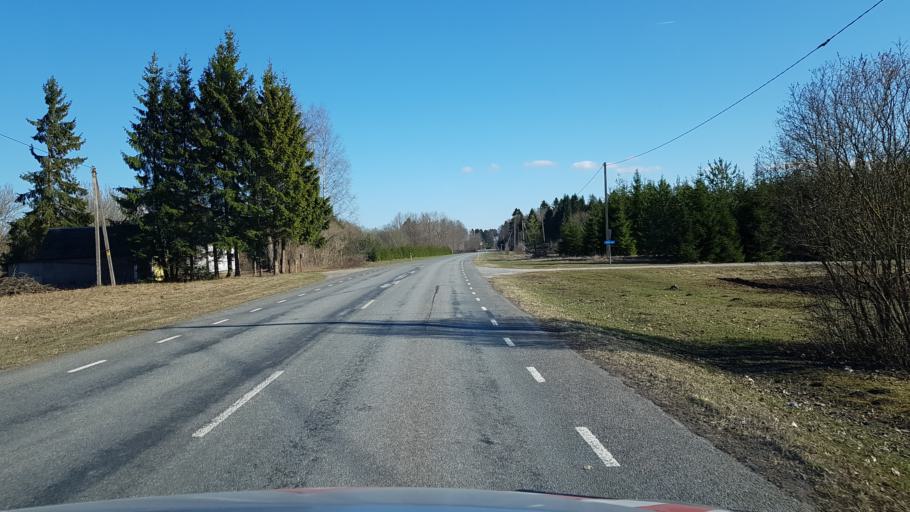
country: EE
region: Laeaene-Virumaa
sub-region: Haljala vald
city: Haljala
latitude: 59.4470
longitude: 26.2498
